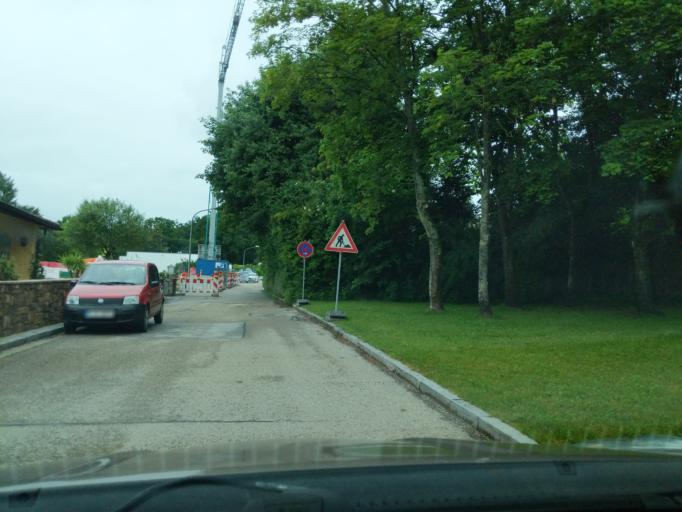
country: DE
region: Bavaria
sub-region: Upper Palatinate
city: Lappersdorf
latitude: 49.0618
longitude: 12.0862
